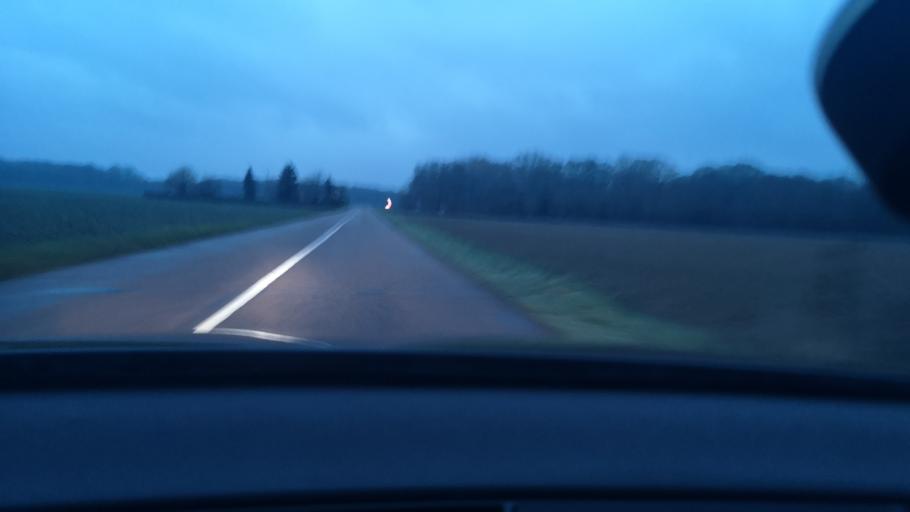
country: FR
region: Bourgogne
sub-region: Departement de Saone-et-Loire
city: Demigny
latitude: 46.9471
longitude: 4.8938
